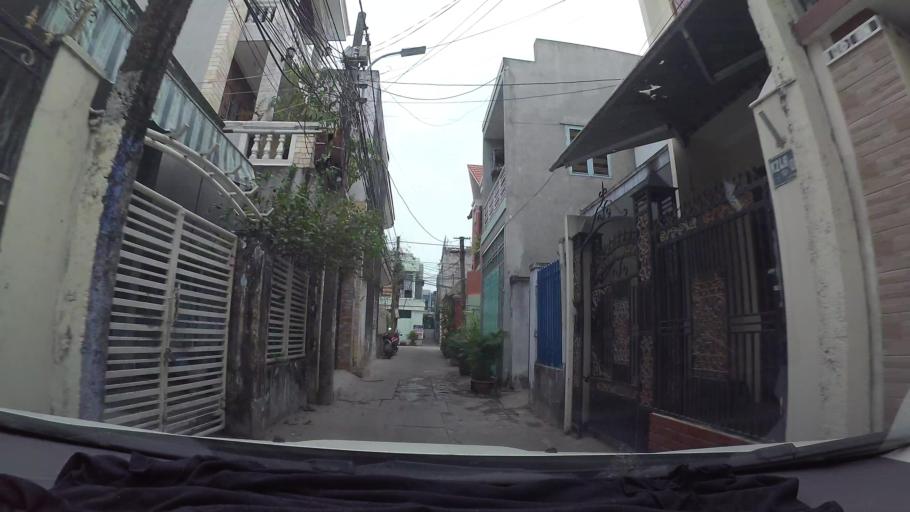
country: VN
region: Da Nang
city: Thanh Khe
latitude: 16.0546
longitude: 108.1831
